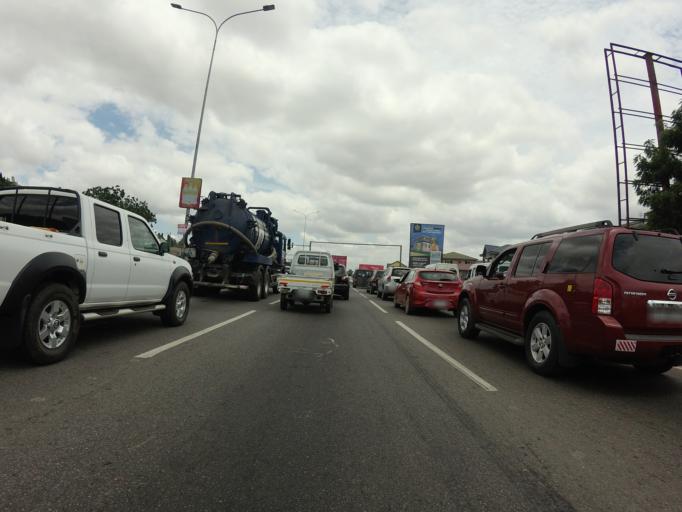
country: GH
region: Greater Accra
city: Gbawe
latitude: 5.5651
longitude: -0.2889
